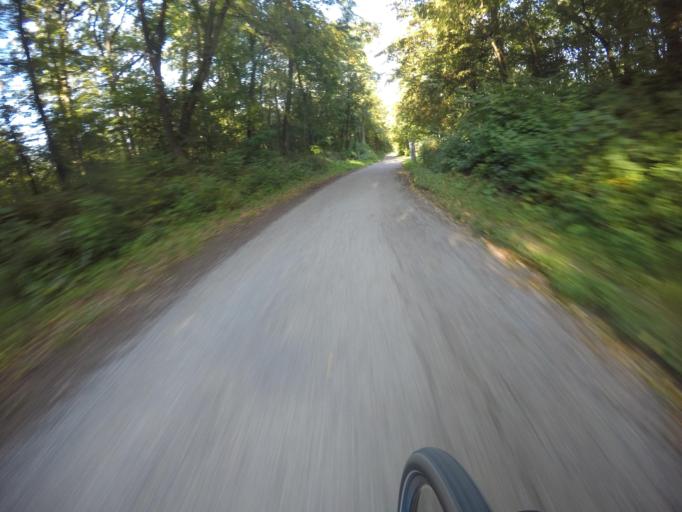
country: DE
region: Baden-Wuerttemberg
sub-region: Regierungsbezirk Stuttgart
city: Stuttgart Feuerbach
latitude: 48.8029
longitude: 9.1349
